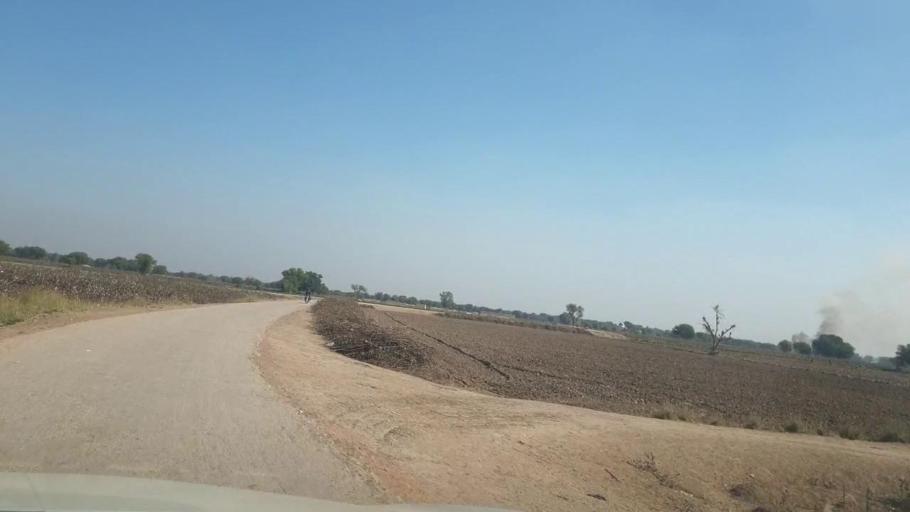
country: PK
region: Sindh
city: Bhan
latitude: 26.5794
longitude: 67.6991
